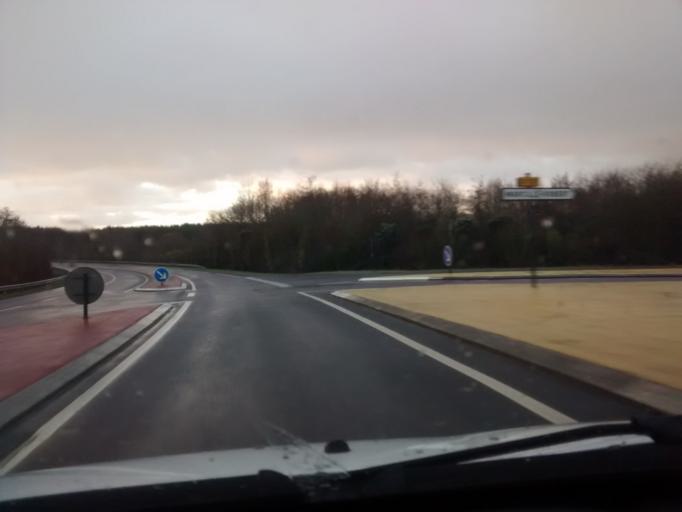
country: FR
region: Brittany
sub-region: Departement d'Ille-et-Vilaine
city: Louvigne-de-Bais
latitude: 48.0297
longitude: -1.3158
